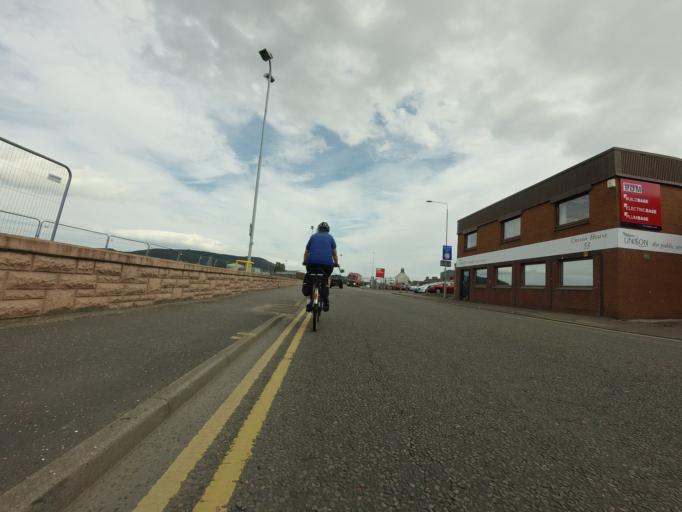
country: GB
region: Scotland
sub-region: Highland
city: Inverness
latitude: 57.4851
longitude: -4.2293
